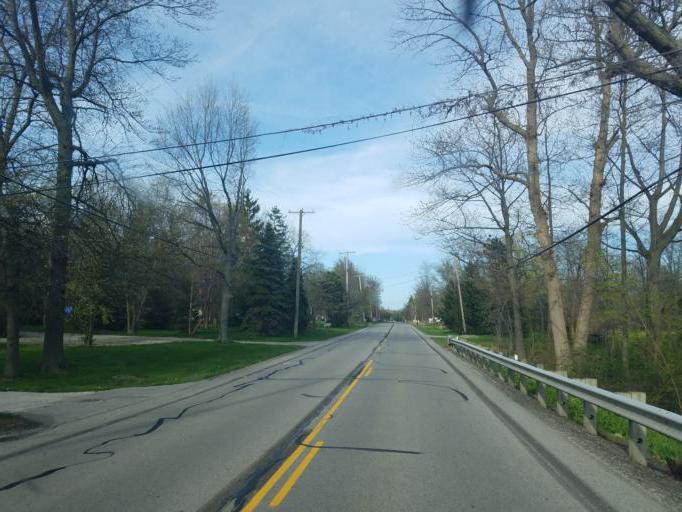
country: US
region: Ohio
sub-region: Ashtabula County
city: Ashtabula
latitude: 41.8775
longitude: -80.8707
